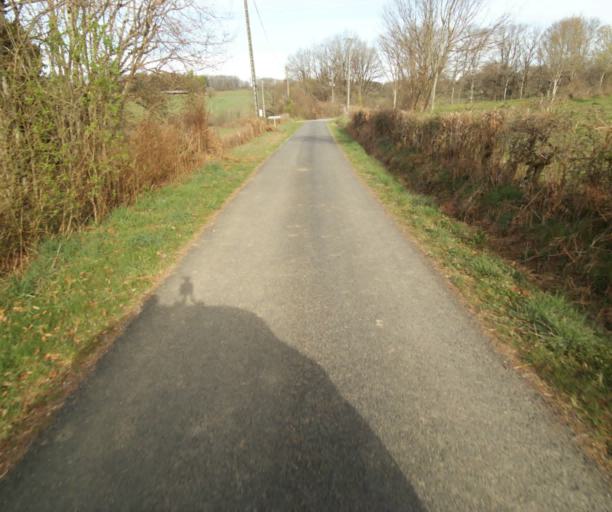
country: FR
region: Limousin
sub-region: Departement de la Correze
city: Chamboulive
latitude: 45.4214
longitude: 1.7620
